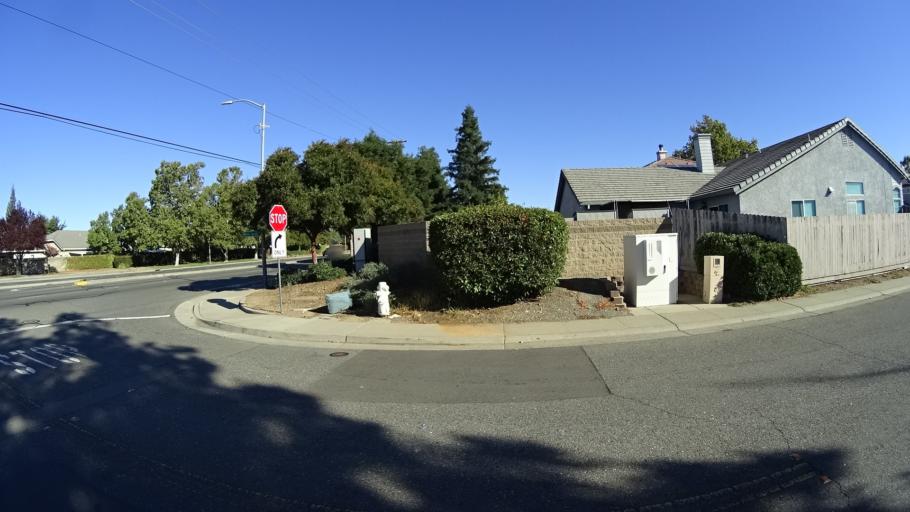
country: US
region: California
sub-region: Sacramento County
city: Vineyard
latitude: 38.4420
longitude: -121.3713
